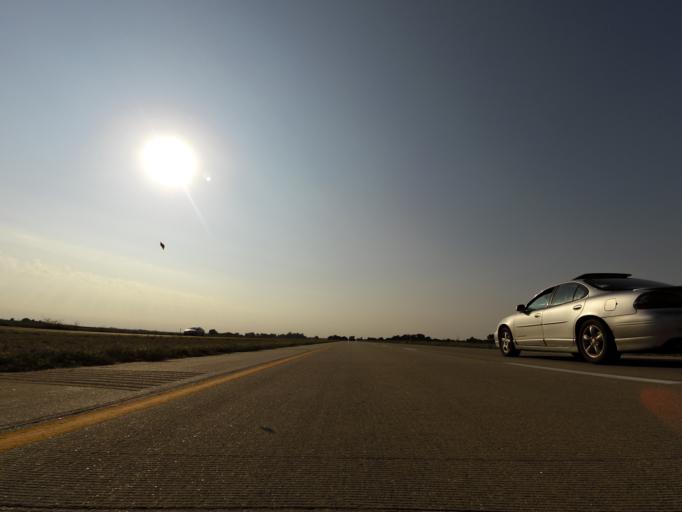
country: US
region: Kansas
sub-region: Sedgwick County
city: Colwich
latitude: 37.8504
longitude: -97.5989
